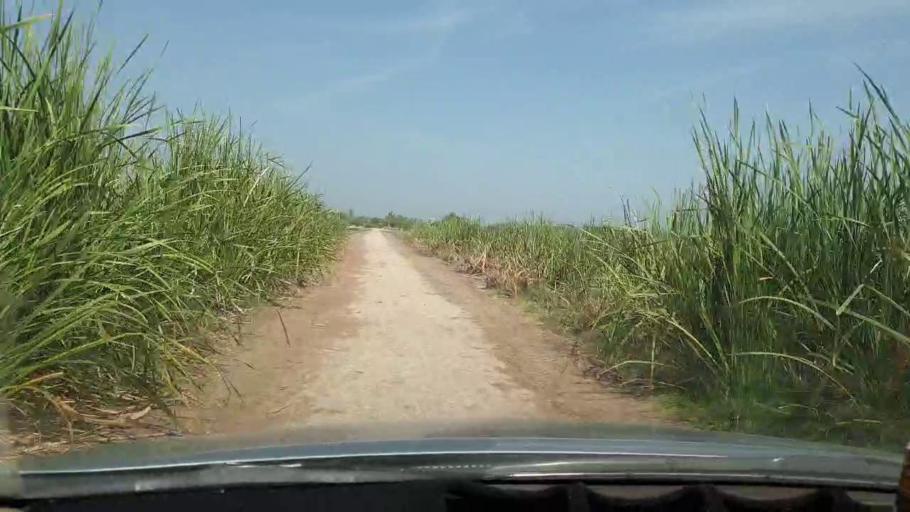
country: PK
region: Sindh
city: Khairpur
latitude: 27.4713
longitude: 68.7447
